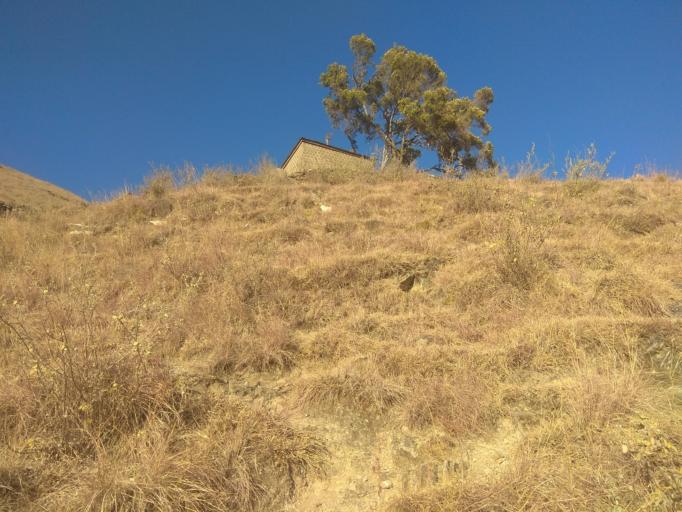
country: NP
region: Mid Western
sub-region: Bheri Zone
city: Dailekh
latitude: 29.2610
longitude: 81.6817
